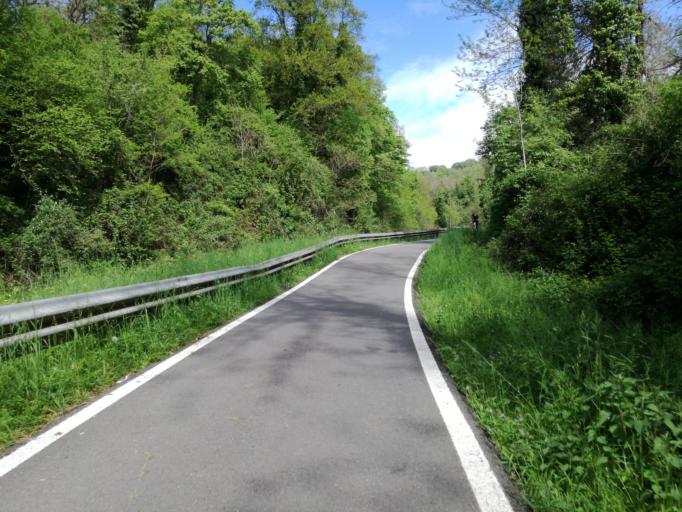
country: IT
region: Lombardy
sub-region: Provincia di Bergamo
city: Calusco d'Adda
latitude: 45.6743
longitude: 9.4668
